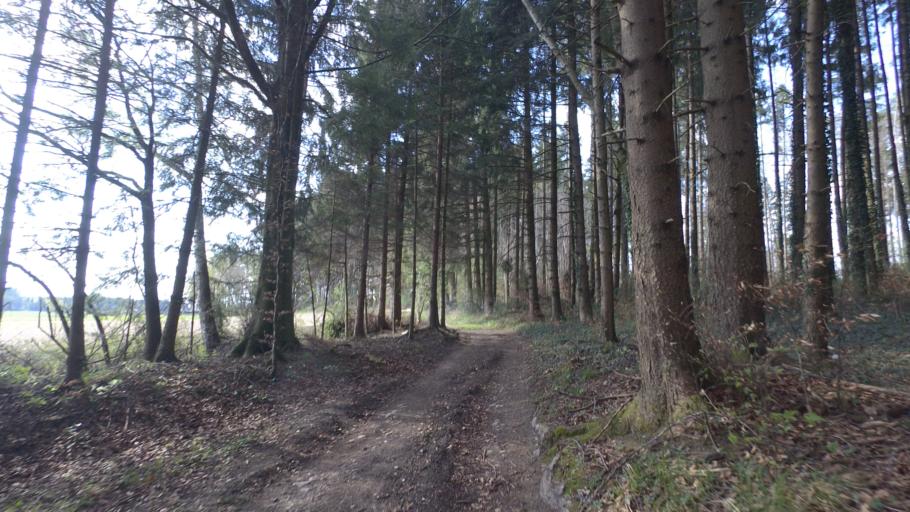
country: DE
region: Bavaria
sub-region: Upper Bavaria
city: Chieming
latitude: 47.9196
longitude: 12.5353
